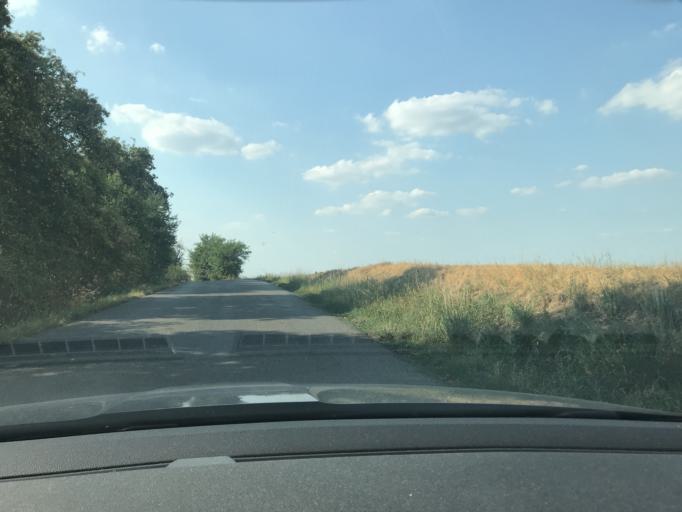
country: CZ
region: Central Bohemia
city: Kralupy nad Vltavou
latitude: 50.2271
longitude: 14.3206
